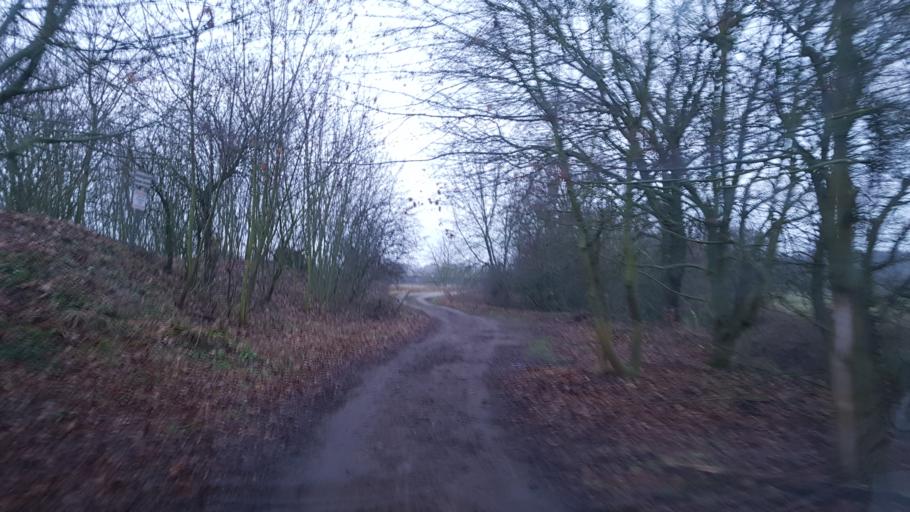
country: DE
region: Brandenburg
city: Stahnsdorf
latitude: 52.3608
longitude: 13.2037
